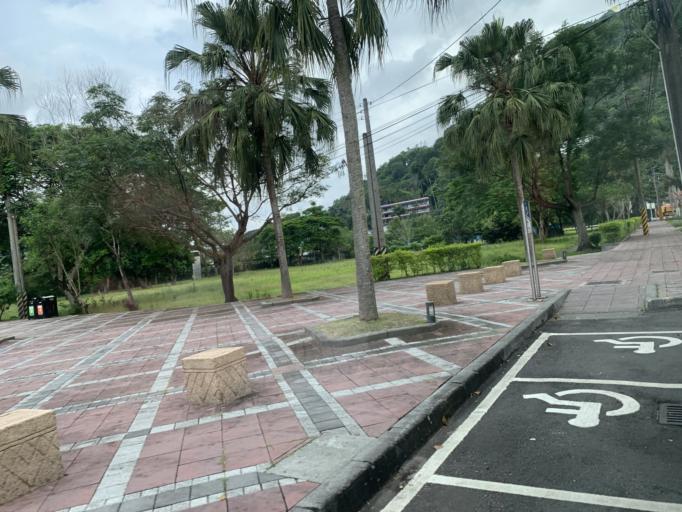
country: TW
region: Taiwan
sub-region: Hualien
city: Hualian
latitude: 23.9350
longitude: 121.5074
